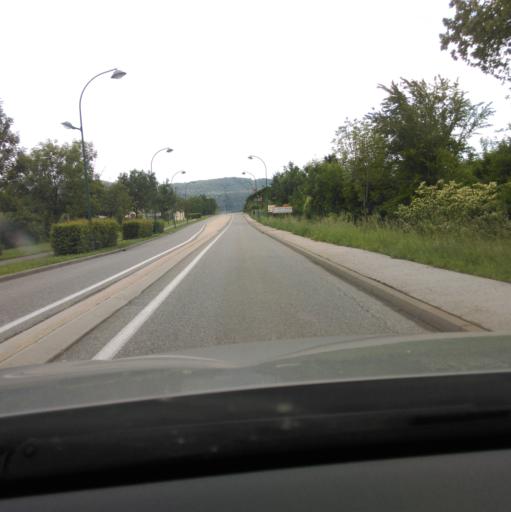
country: FR
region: Rhone-Alpes
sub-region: Departement de l'Ain
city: Montreal-la-Cluse
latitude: 46.1768
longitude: 5.5575
